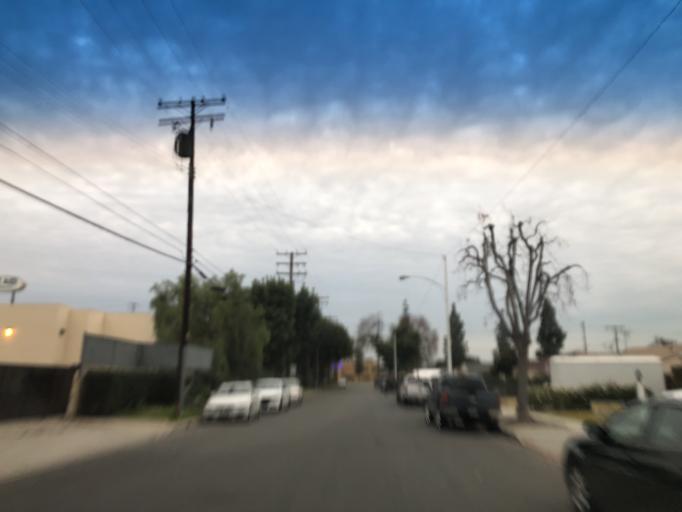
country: US
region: California
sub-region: Los Angeles County
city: Citrus
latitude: 34.1153
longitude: -117.9057
